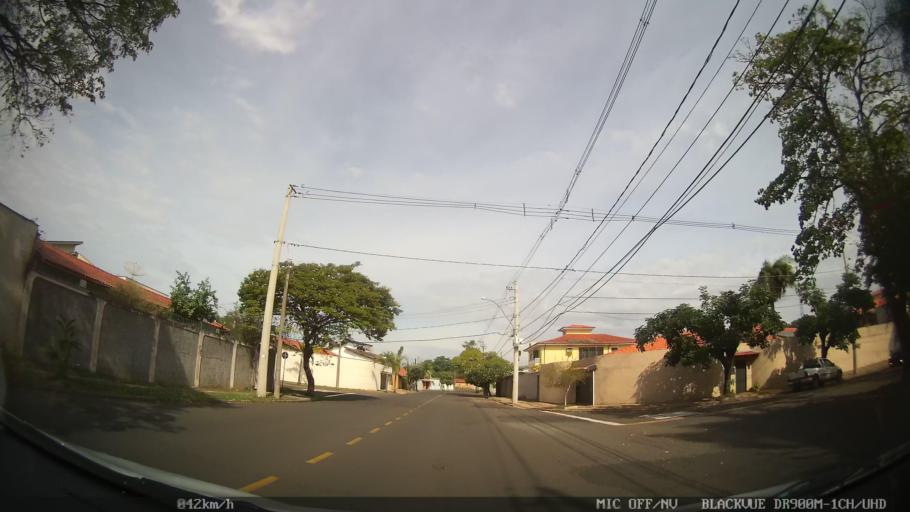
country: BR
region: Sao Paulo
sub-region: Piracicaba
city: Piracicaba
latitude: -22.7103
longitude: -47.6729
